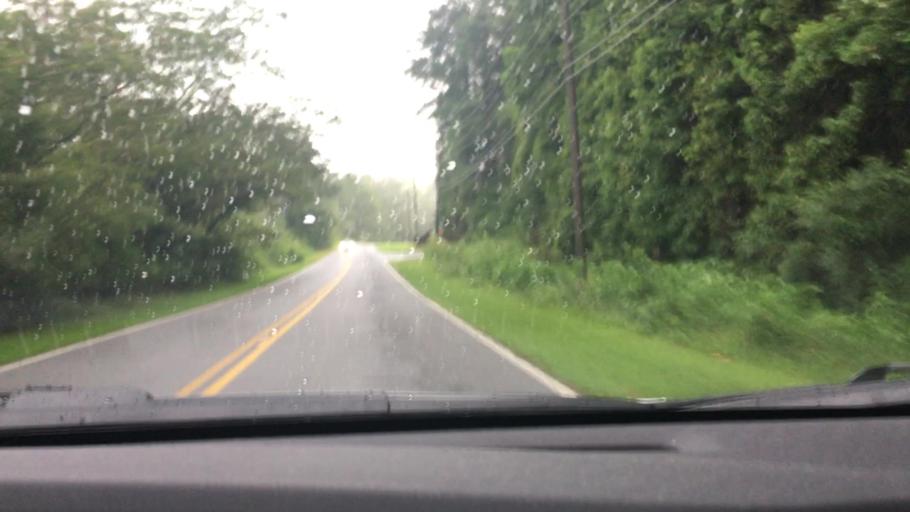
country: US
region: Georgia
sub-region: Fulton County
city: Union City
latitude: 33.6388
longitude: -84.5252
